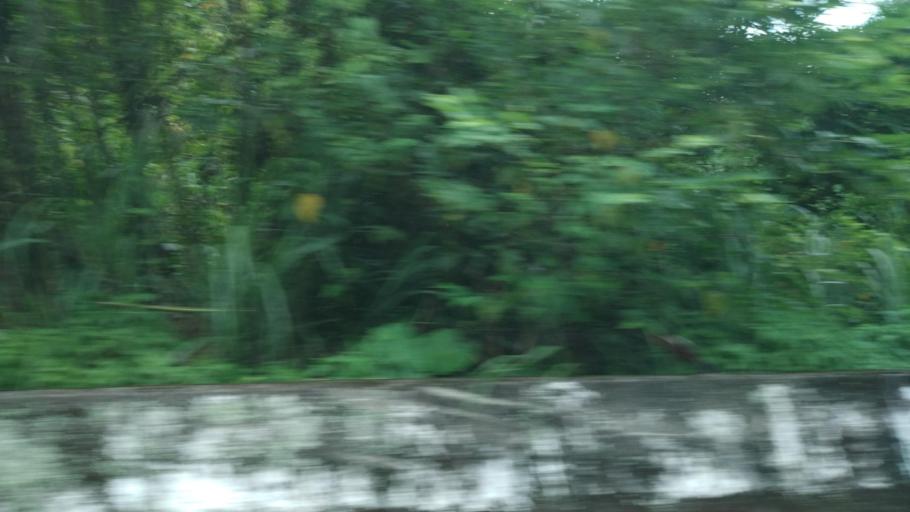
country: TW
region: Taipei
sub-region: Taipei
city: Banqiao
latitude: 24.9262
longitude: 121.4381
